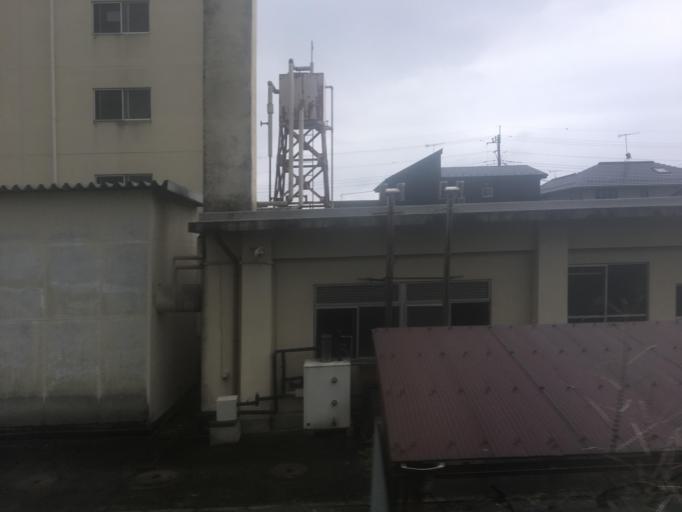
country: JP
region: Saitama
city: Yorii
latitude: 36.1330
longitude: 139.2540
